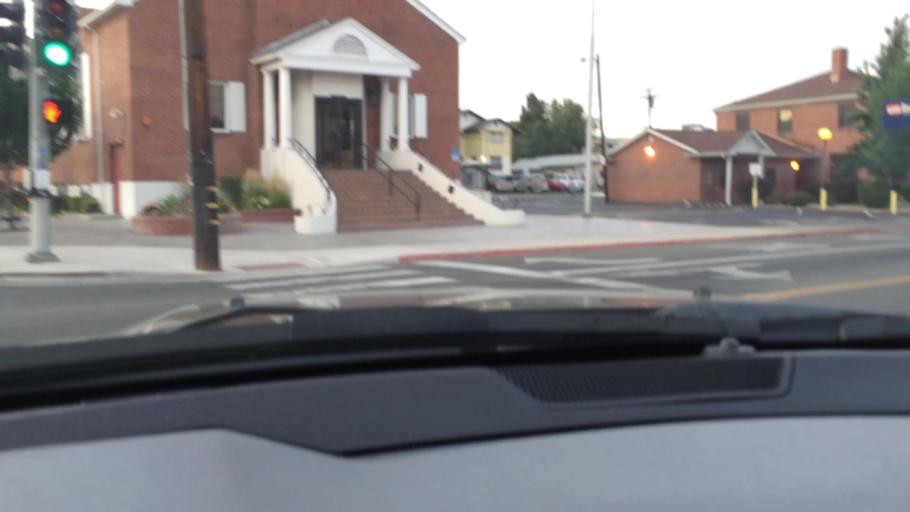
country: US
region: Nevada
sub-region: Washoe County
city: Reno
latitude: 39.5128
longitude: -119.8031
